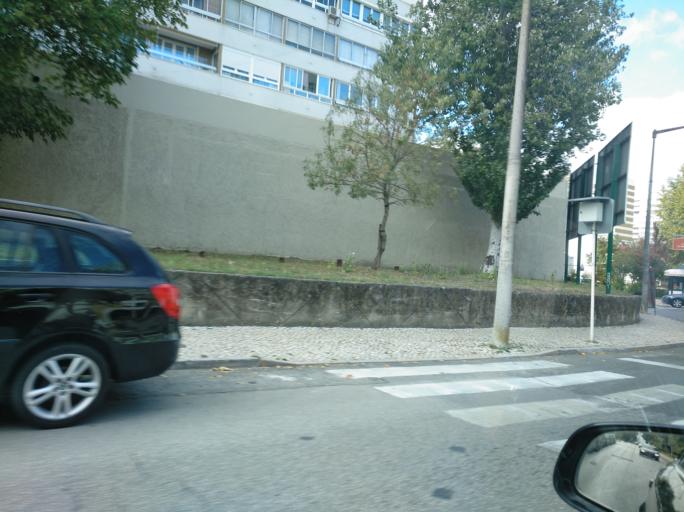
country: PT
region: Lisbon
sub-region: Loures
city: Moscavide
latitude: 38.7808
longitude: -9.1111
